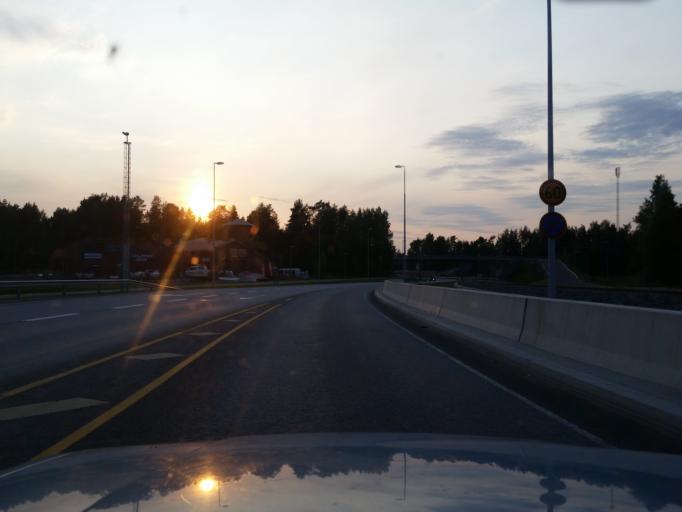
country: FI
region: Southern Savonia
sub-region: Savonlinna
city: Savonlinna
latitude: 61.8767
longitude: 28.8746
